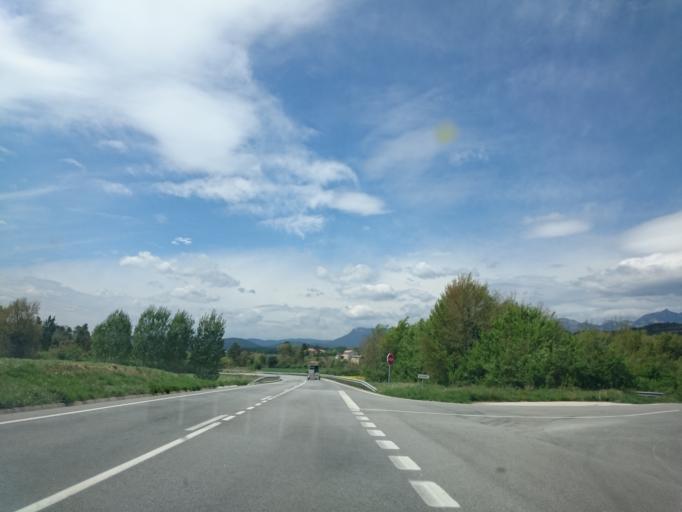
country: ES
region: Catalonia
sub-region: Provincia de Barcelona
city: Olvan
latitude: 42.0520
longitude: 1.9137
